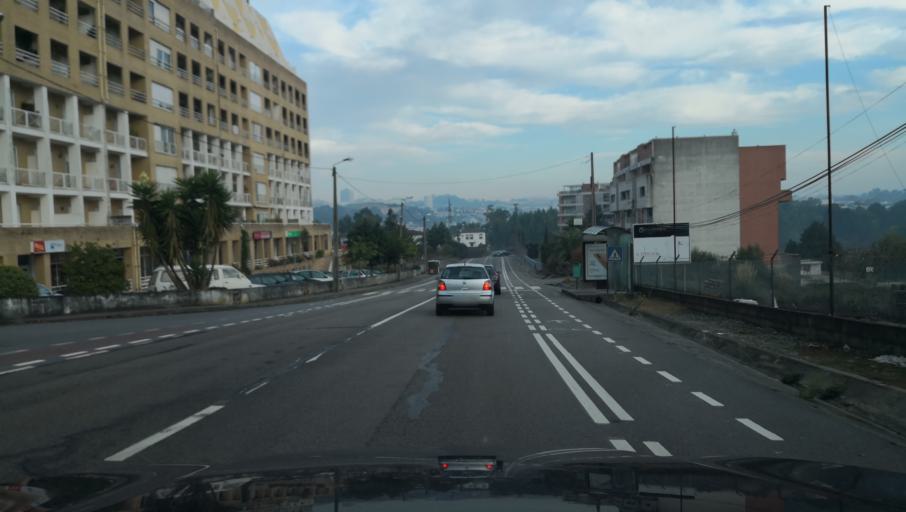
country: PT
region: Porto
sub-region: Gondomar
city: Valbom
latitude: 41.1447
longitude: -8.5670
